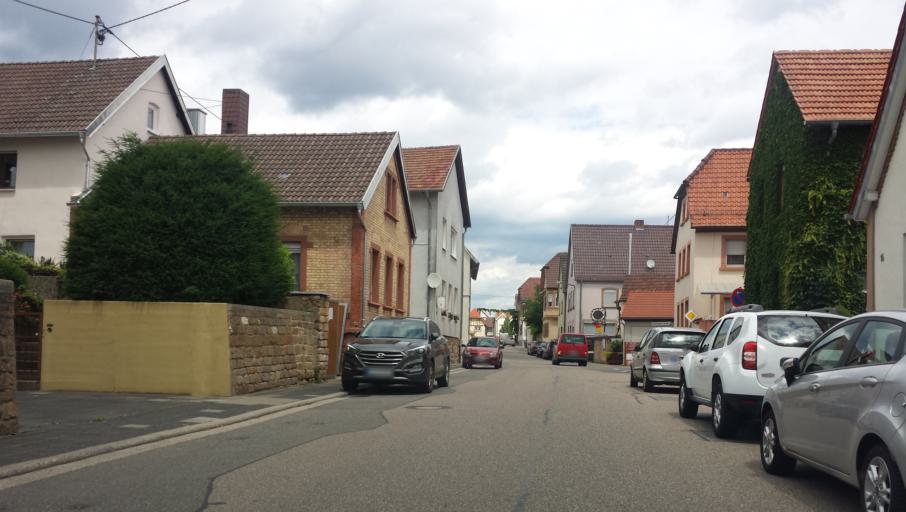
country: DE
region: Rheinland-Pfalz
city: Landau in der Pfalz
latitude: 49.2208
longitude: 8.1103
